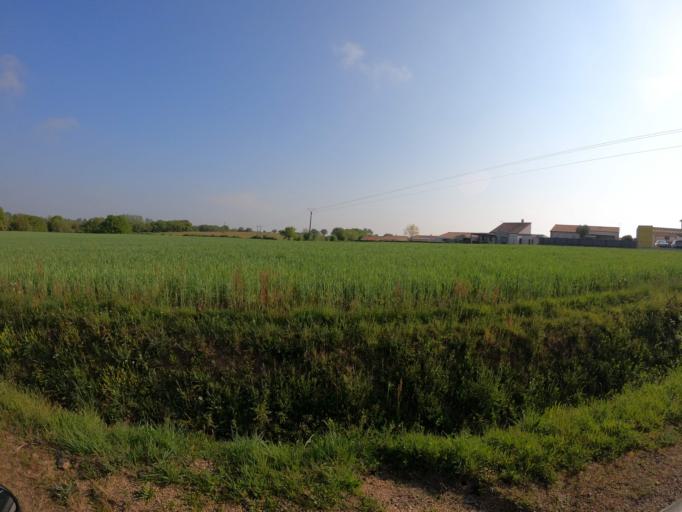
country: FR
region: Pays de la Loire
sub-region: Departement de Maine-et-Loire
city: La Seguiniere
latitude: 47.0673
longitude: -0.9547
